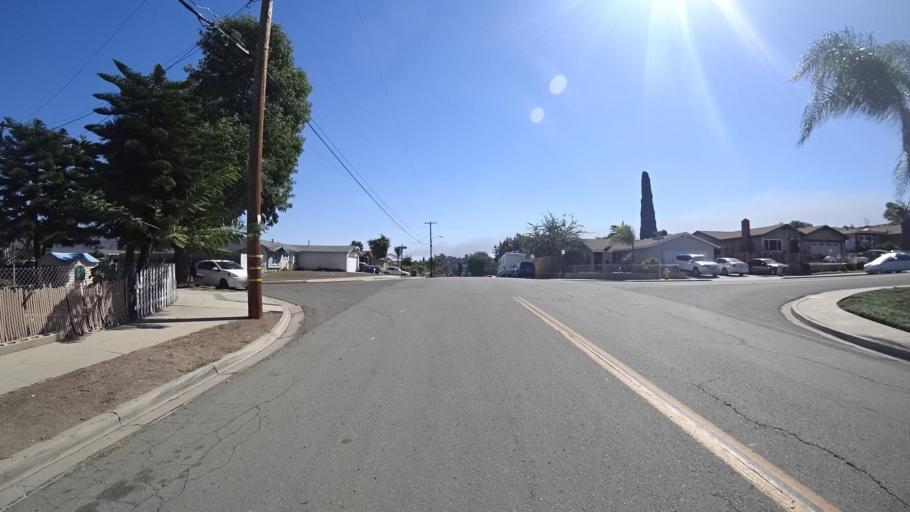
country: US
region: California
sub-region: San Diego County
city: La Presa
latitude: 32.7115
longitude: -117.0192
